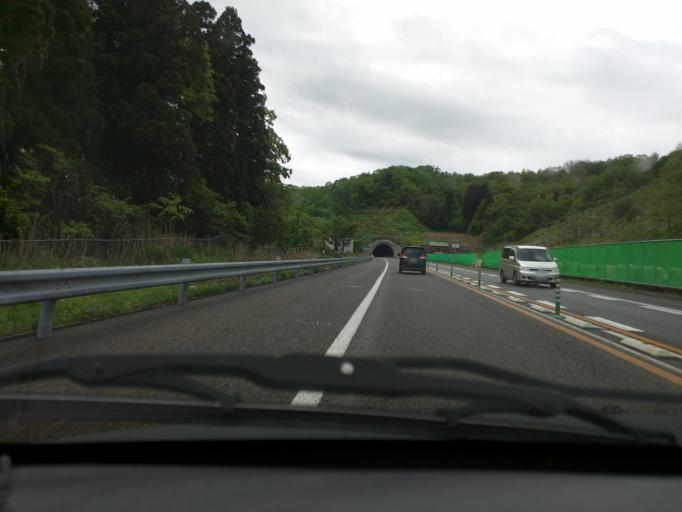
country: JP
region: Niigata
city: Joetsu
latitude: 37.1086
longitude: 138.2193
